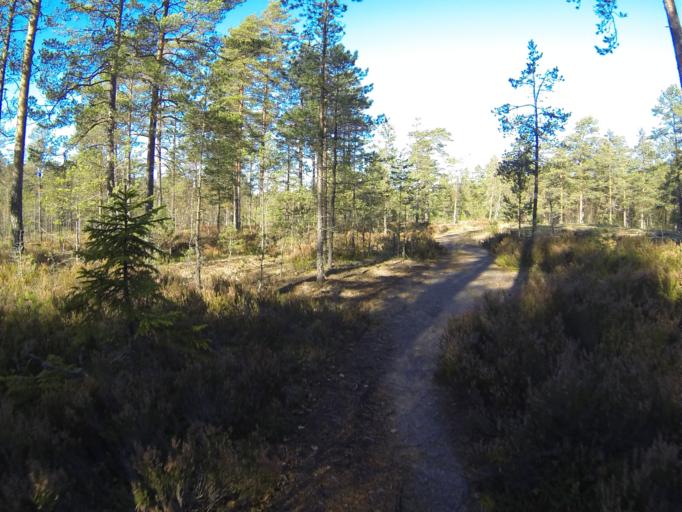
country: FI
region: Varsinais-Suomi
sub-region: Salo
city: Saerkisalo
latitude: 60.2021
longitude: 22.9237
